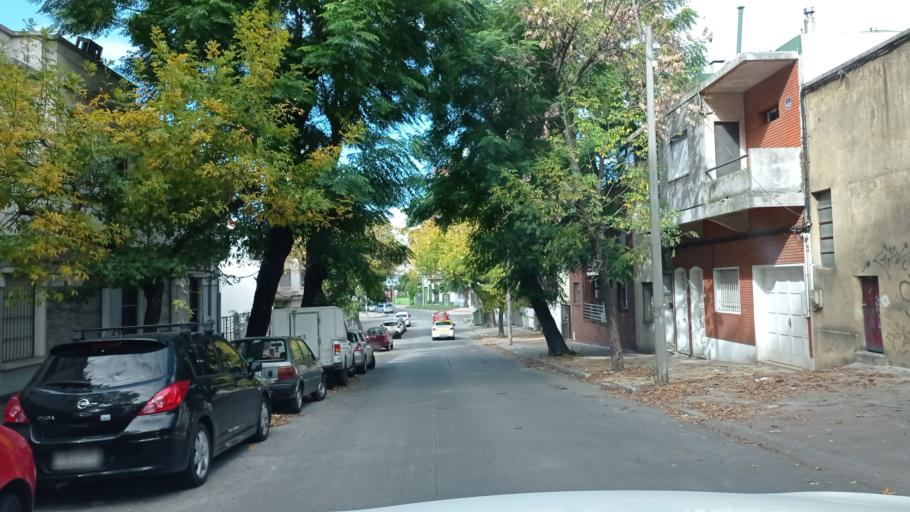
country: UY
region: Montevideo
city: Montevideo
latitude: -34.9049
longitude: -56.1526
